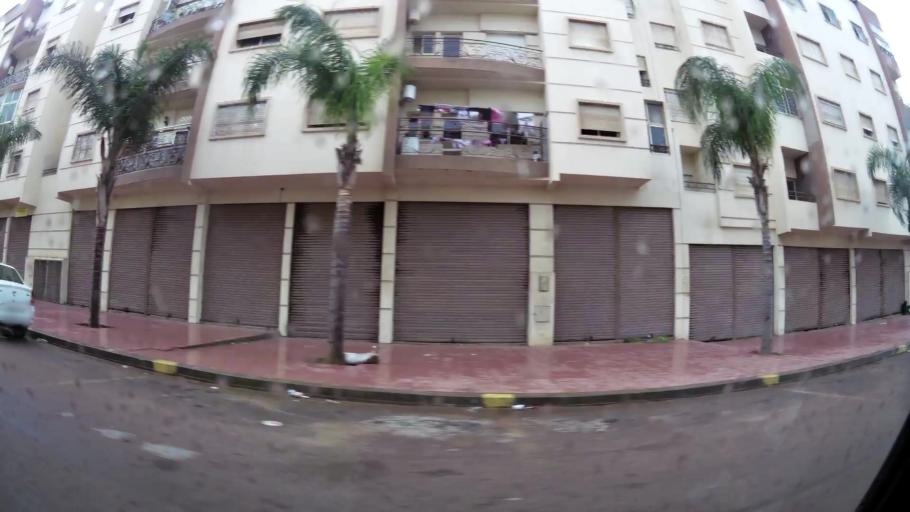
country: MA
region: Grand Casablanca
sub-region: Casablanca
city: Casablanca
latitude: 33.5513
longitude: -7.6939
